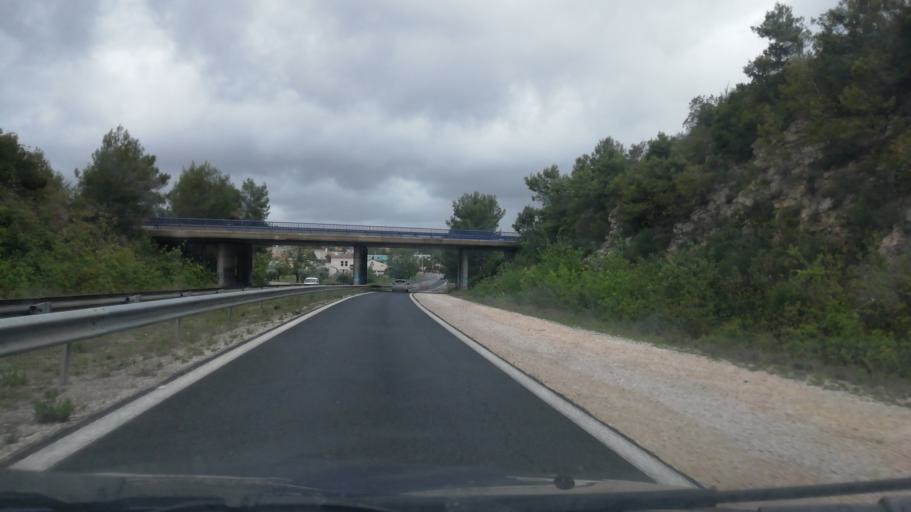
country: FR
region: Languedoc-Roussillon
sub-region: Departement de l'Herault
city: Saint-Clement-de-Riviere
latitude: 43.6733
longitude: 3.8197
